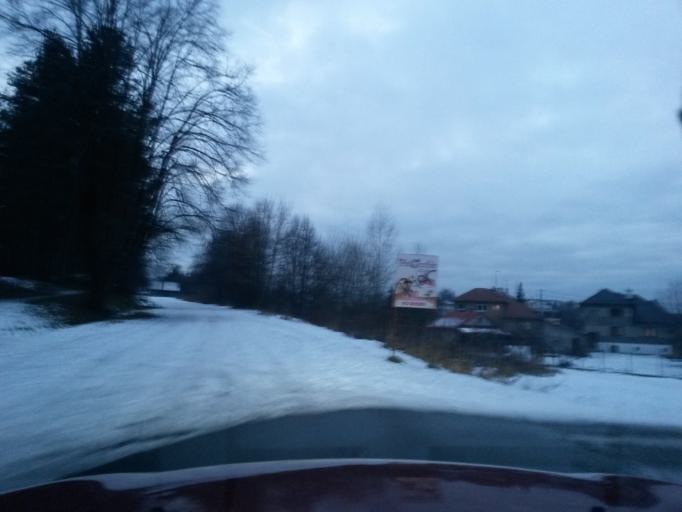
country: SK
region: Kosicky
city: Spisska Nova Ves
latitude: 48.9372
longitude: 20.5597
